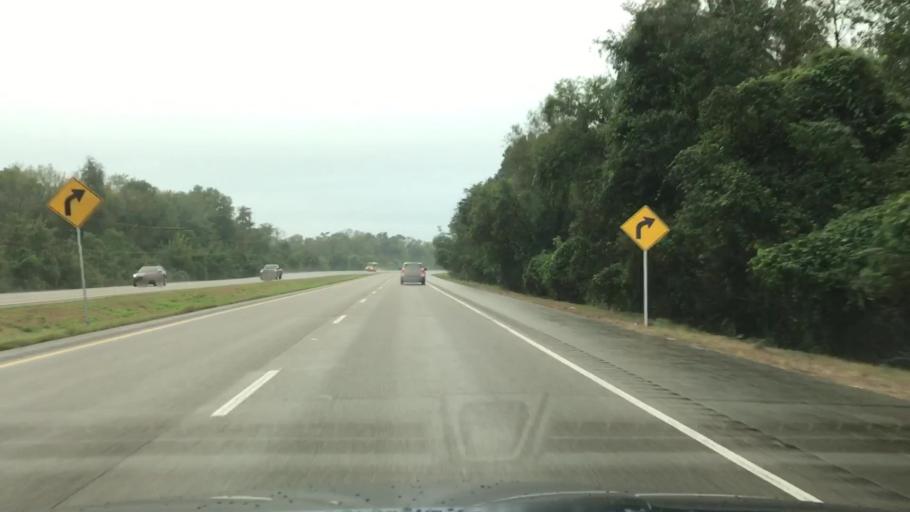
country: US
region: Louisiana
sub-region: Saint Charles Parish
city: Des Allemands
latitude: 29.8469
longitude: -90.4480
